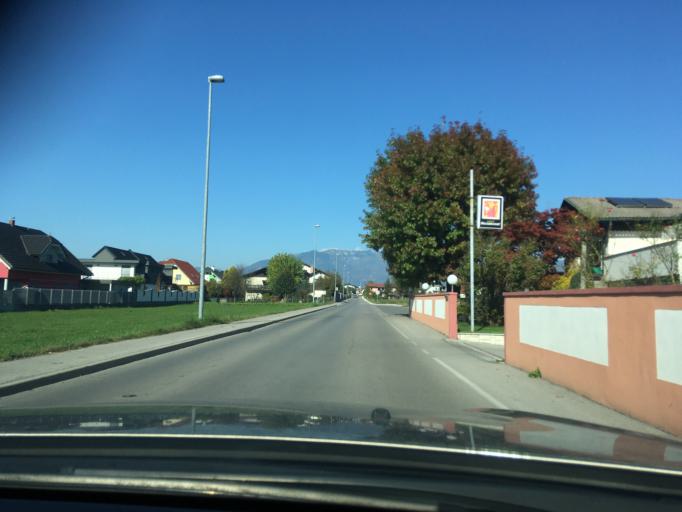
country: SI
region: Domzale
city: Vir
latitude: 46.1446
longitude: 14.6085
